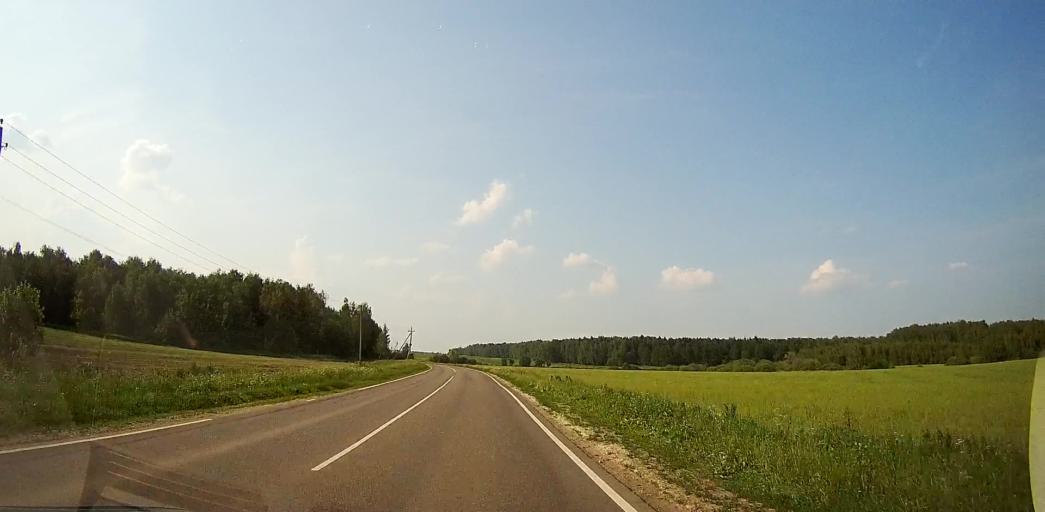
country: RU
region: Moskovskaya
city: Yakovlevskoye
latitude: 55.4571
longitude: 37.9807
